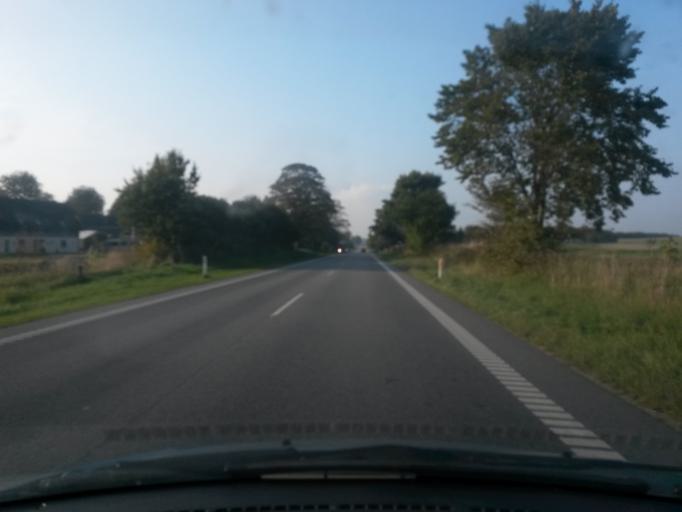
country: DK
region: Central Jutland
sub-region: Syddjurs Kommune
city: Hornslet
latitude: 56.3601
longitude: 10.3352
